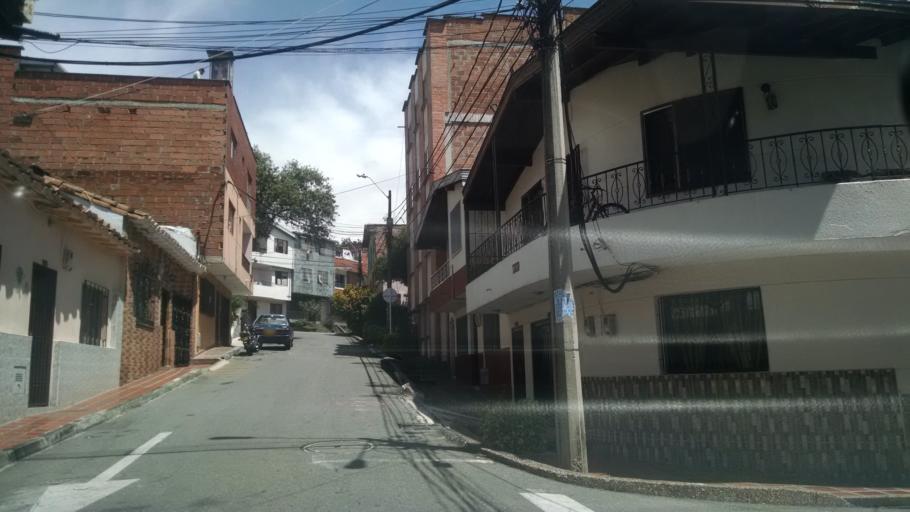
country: CO
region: Antioquia
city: Medellin
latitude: 6.2601
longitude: -75.6071
